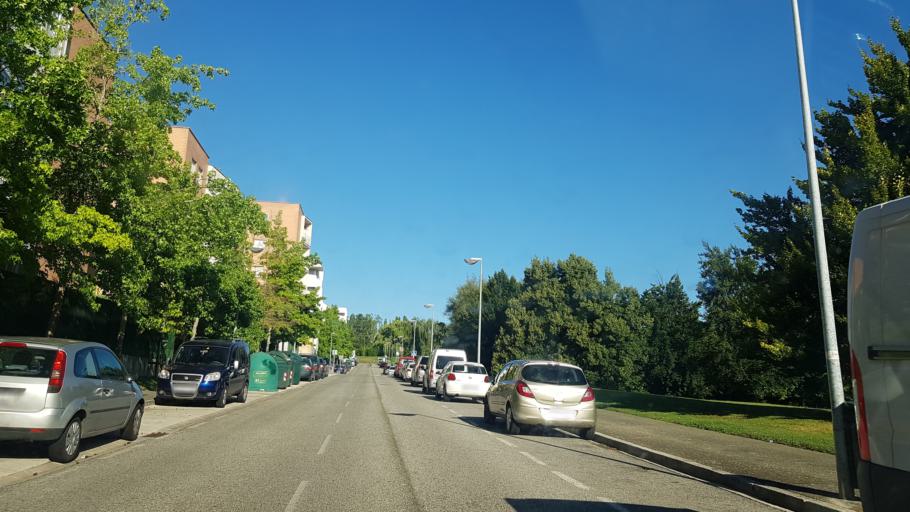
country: ES
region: Navarre
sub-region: Provincia de Navarra
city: Burlata
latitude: 42.8094
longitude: -1.6124
